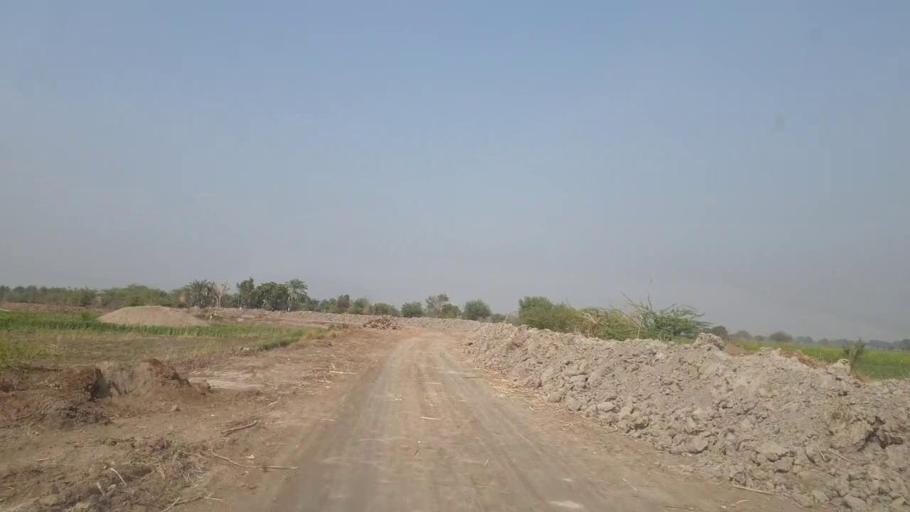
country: PK
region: Sindh
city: Mirpur Khas
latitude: 25.5662
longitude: 69.1431
